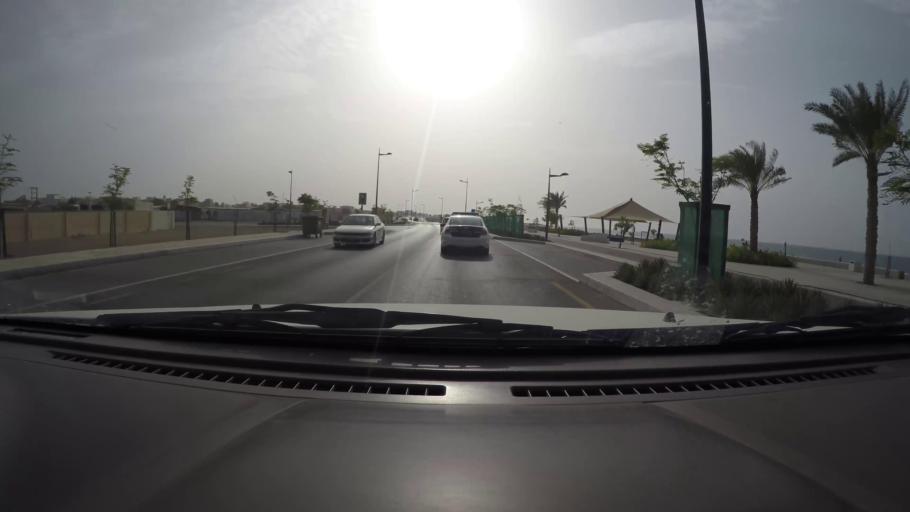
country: OM
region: Muhafazat Masqat
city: As Sib al Jadidah
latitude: 23.6961
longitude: 58.1533
